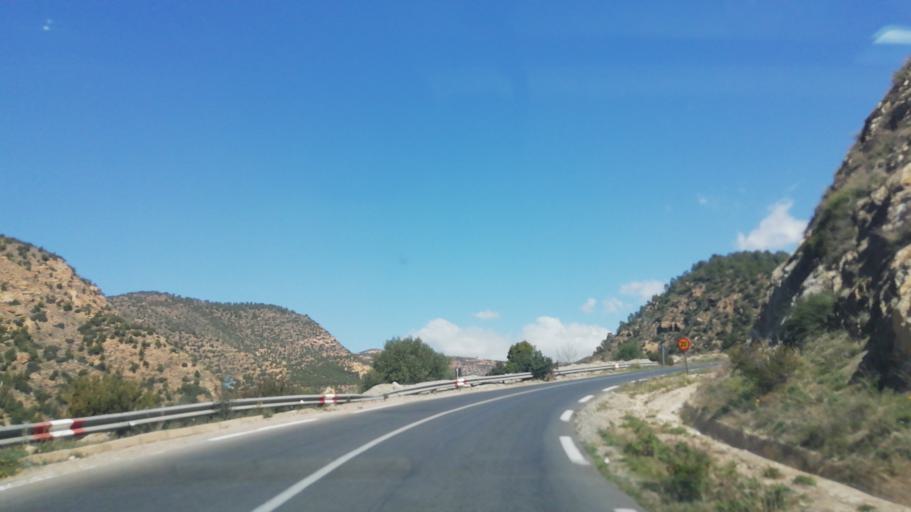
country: DZ
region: Mascara
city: Mascara
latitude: 35.5007
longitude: 0.1295
